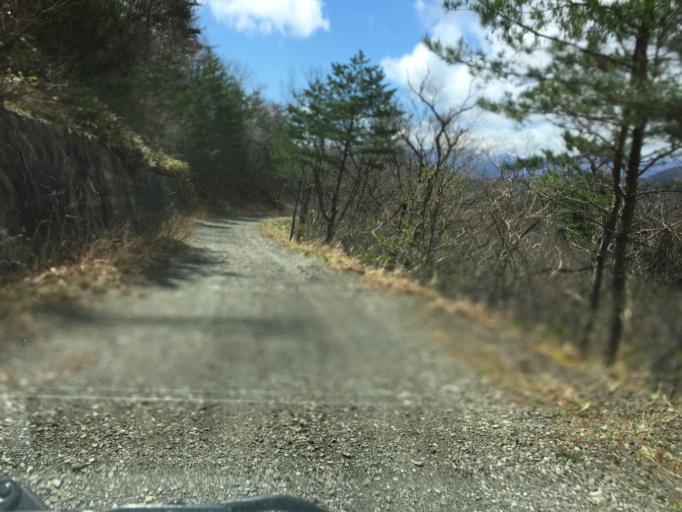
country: JP
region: Fukushima
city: Fukushima-shi
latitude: 37.8566
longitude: 140.4168
